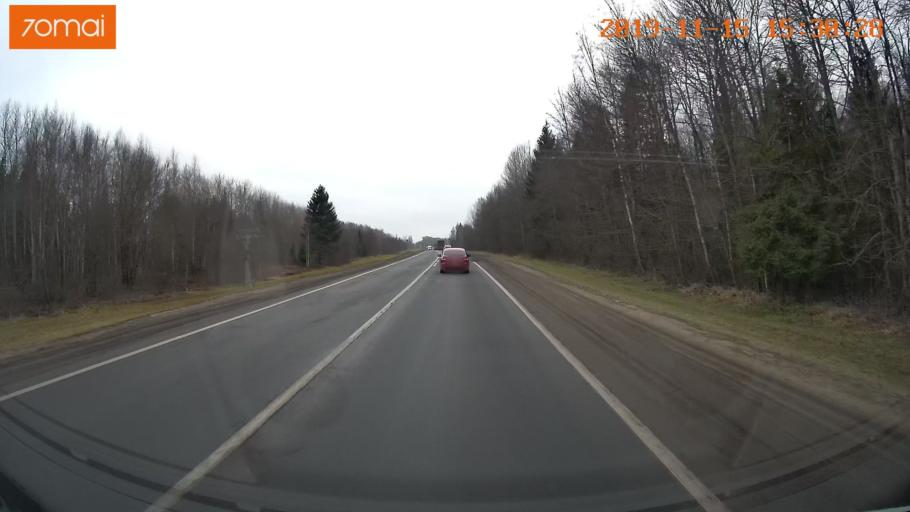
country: RU
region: Jaroslavl
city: Danilov
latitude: 58.1098
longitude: 40.1129
